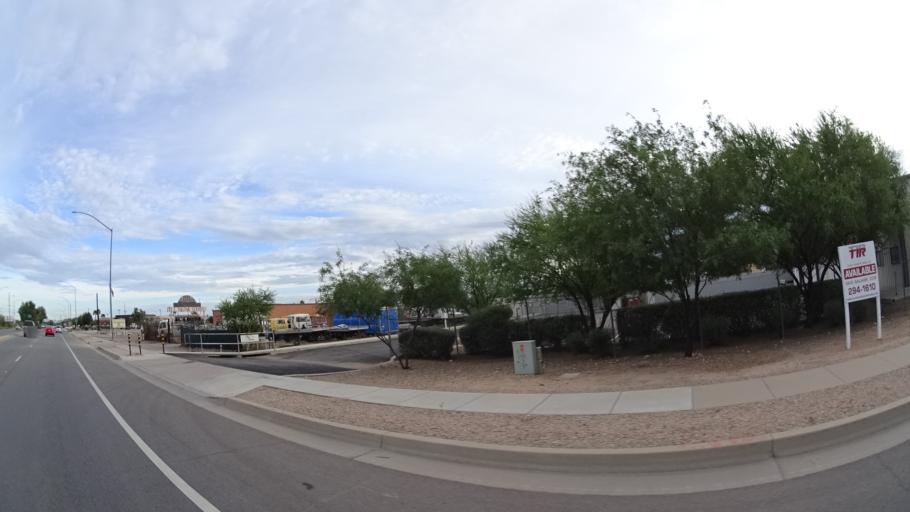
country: US
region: Arizona
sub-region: Pima County
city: South Tucson
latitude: 32.1652
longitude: -110.9389
